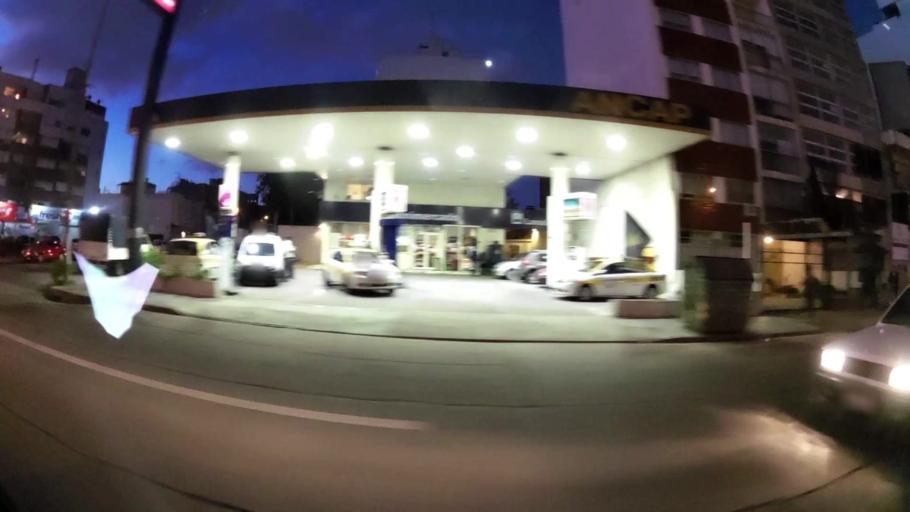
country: UY
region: Montevideo
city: Montevideo
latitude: -34.8903
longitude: -56.1517
